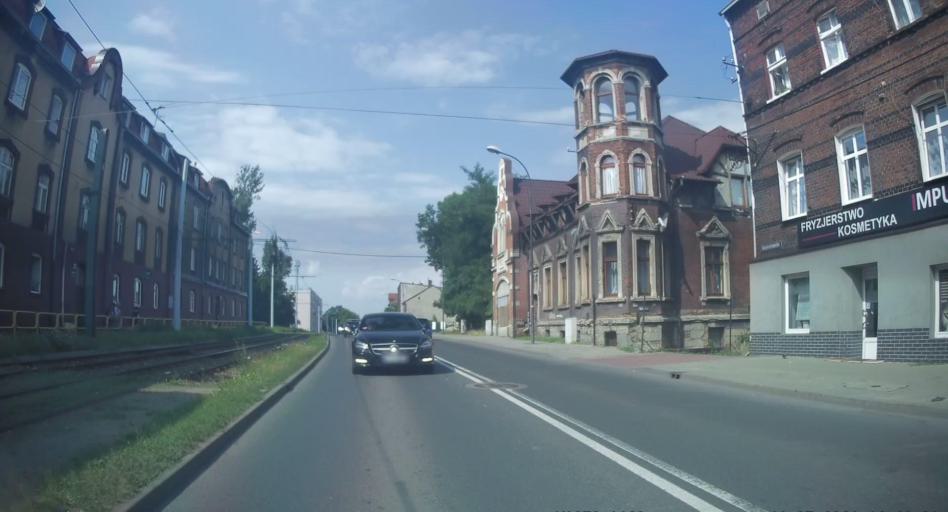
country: PL
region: Silesian Voivodeship
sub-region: Swietochlowice
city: Swietochlowice
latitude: 50.3216
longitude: 18.9268
